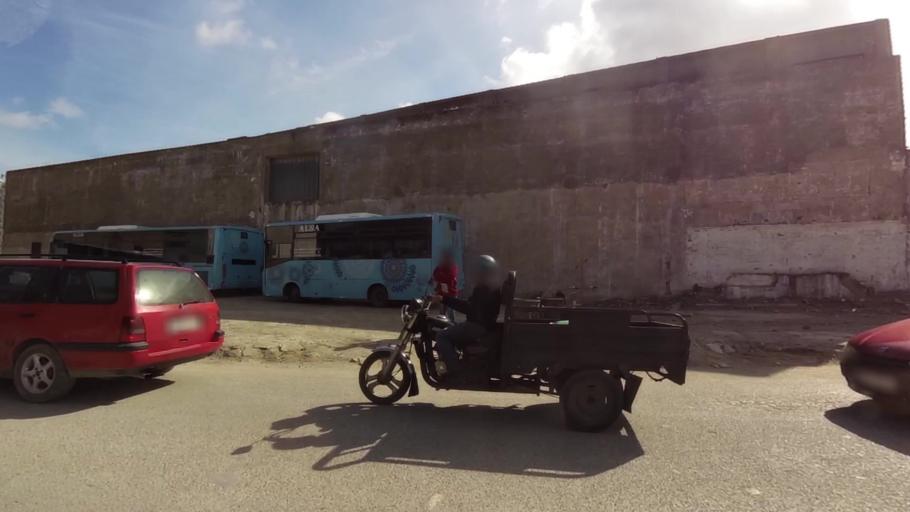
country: MA
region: Tanger-Tetouan
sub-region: Tanger-Assilah
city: Tangier
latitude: 35.7704
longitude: -5.7845
